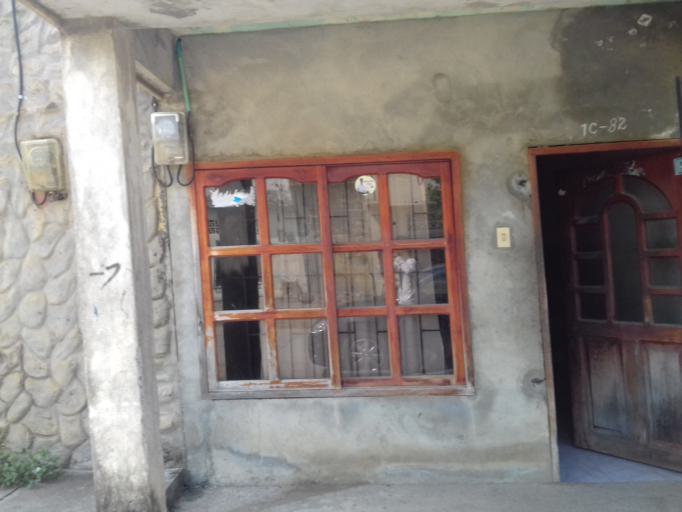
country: CO
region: Cordoba
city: Monteria
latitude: 8.7674
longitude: -75.8790
